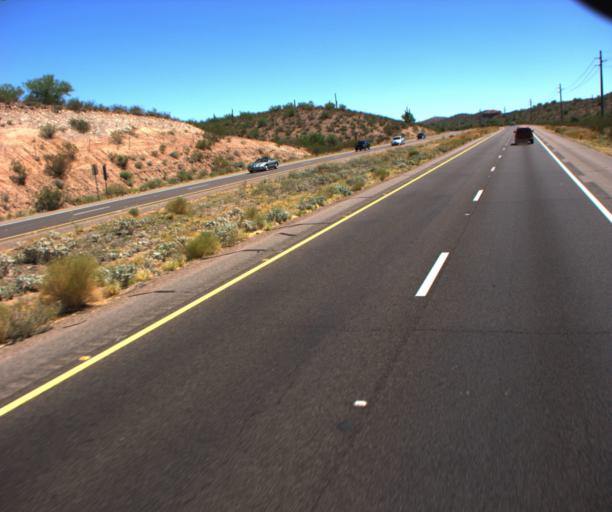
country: US
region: Arizona
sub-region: Maricopa County
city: Fountain Hills
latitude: 33.5311
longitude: -111.7305
